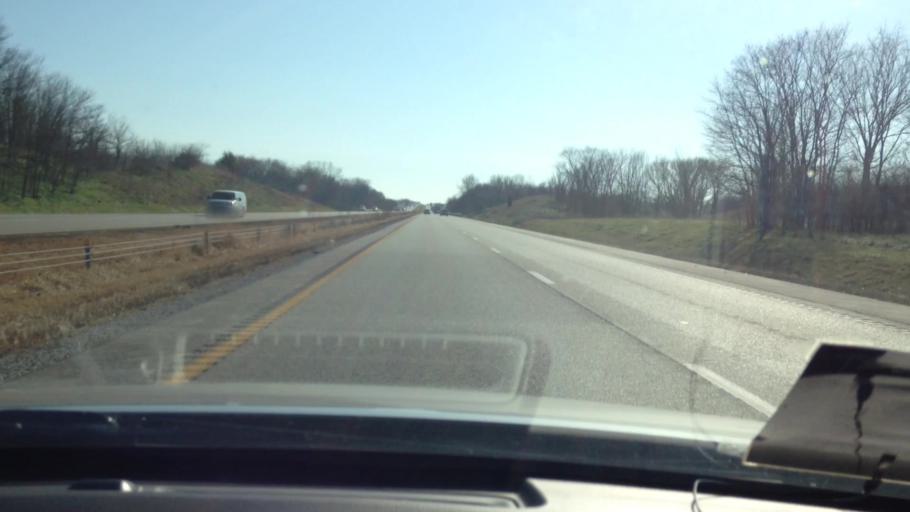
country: US
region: Missouri
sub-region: Platte County
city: Platte City
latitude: 39.4893
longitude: -94.7866
